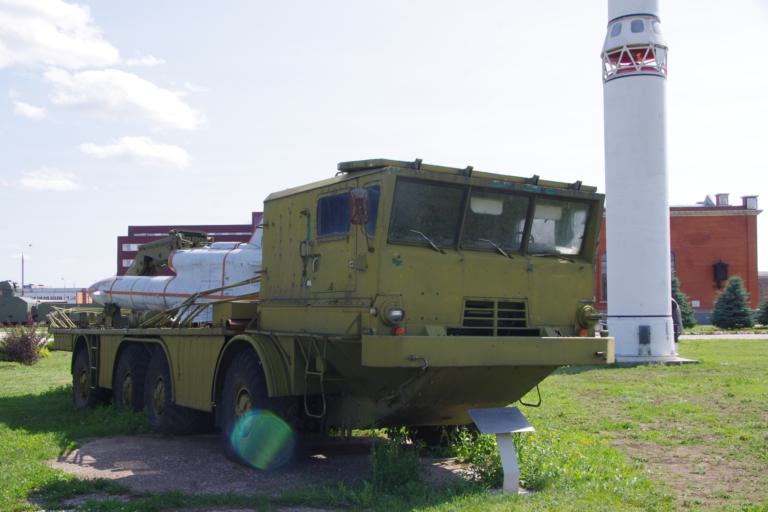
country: RU
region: Samara
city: Tol'yatti
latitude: 53.5523
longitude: 49.2579
